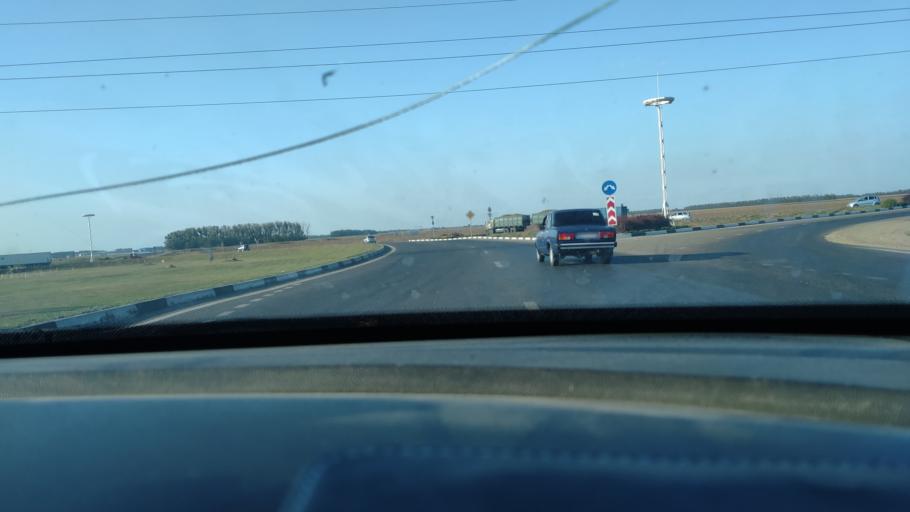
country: RU
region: Krasnodarskiy
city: Timashevsk
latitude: 45.6261
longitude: 38.9857
